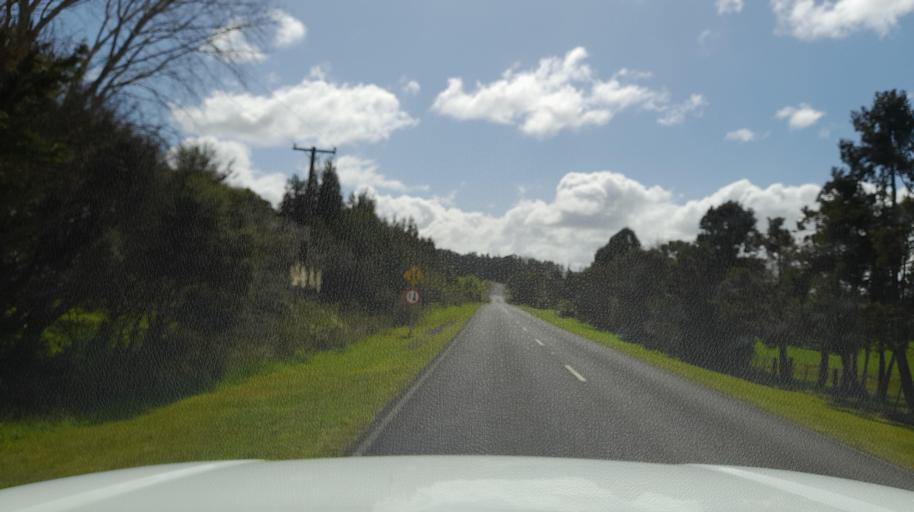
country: NZ
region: Northland
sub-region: Far North District
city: Kerikeri
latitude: -35.2301
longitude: 173.8765
